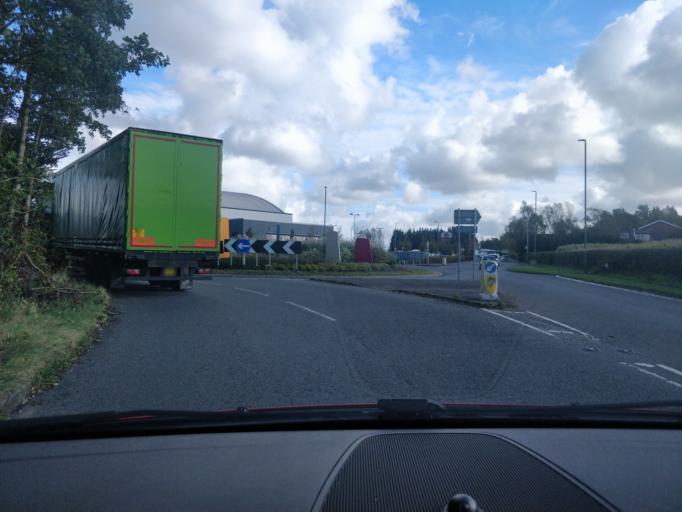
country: GB
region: England
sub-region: Lancashire
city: Ormskirk
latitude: 53.5878
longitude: -2.8669
